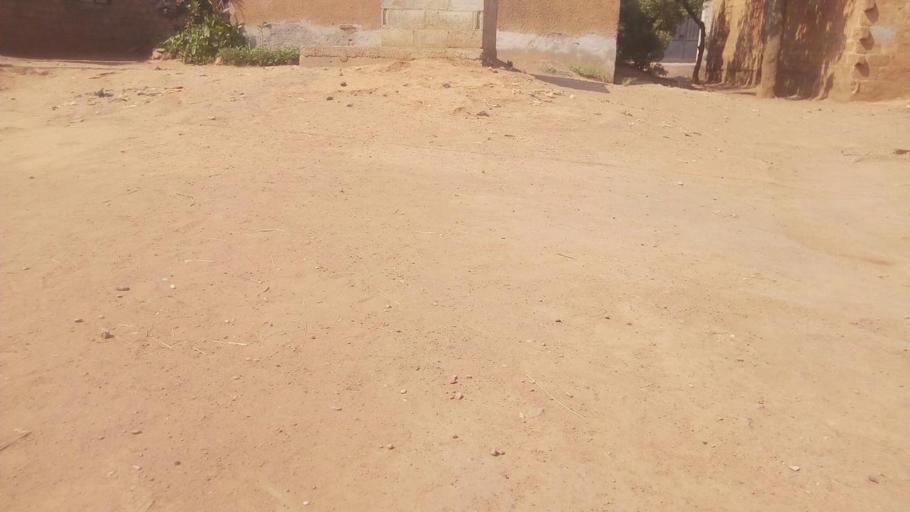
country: ZM
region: Lusaka
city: Lusaka
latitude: -15.3595
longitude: 28.2917
